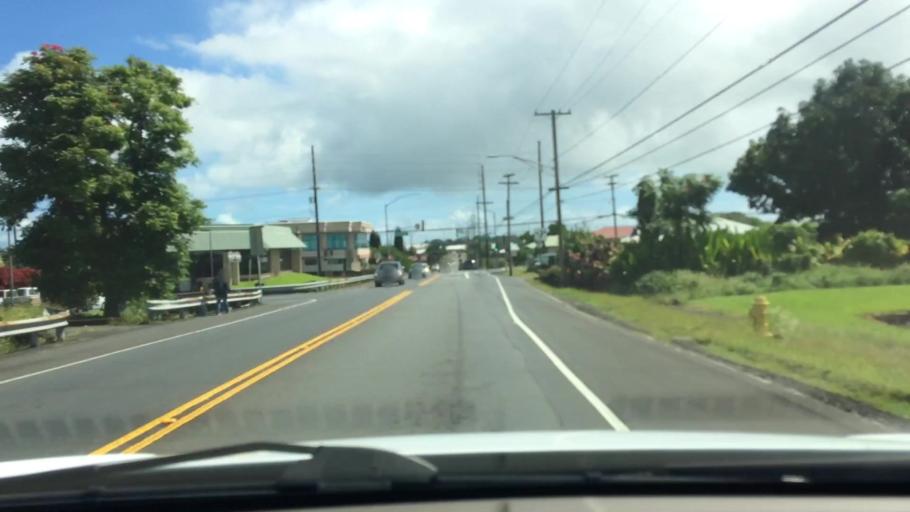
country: US
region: Hawaii
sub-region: Hawaii County
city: Hilo
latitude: 19.7020
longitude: -155.0755
